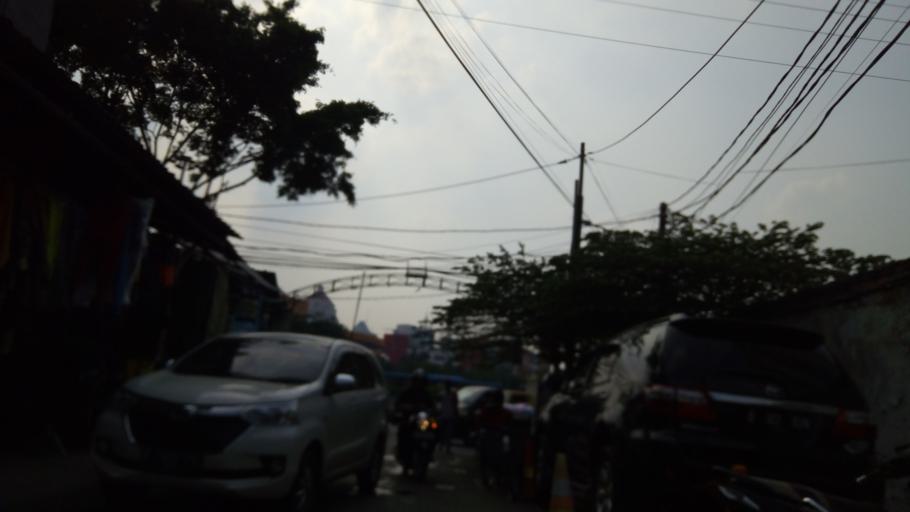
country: ID
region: Jakarta Raya
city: Jakarta
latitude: -6.1771
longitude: 106.8445
